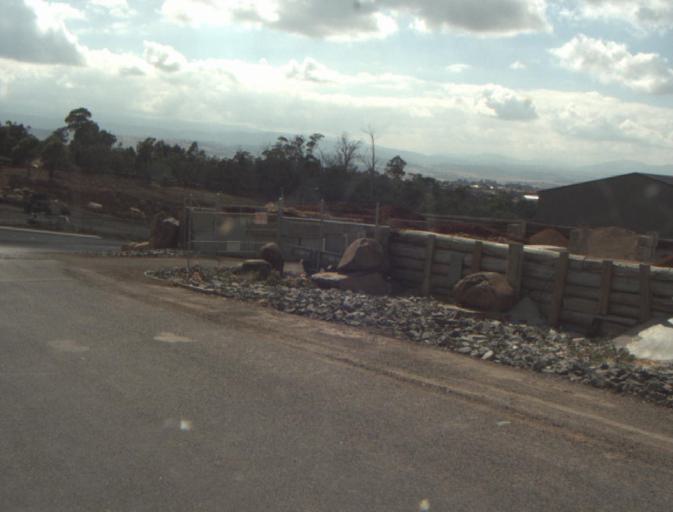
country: AU
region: Tasmania
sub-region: Launceston
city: Summerhill
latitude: -41.4780
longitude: 147.1518
